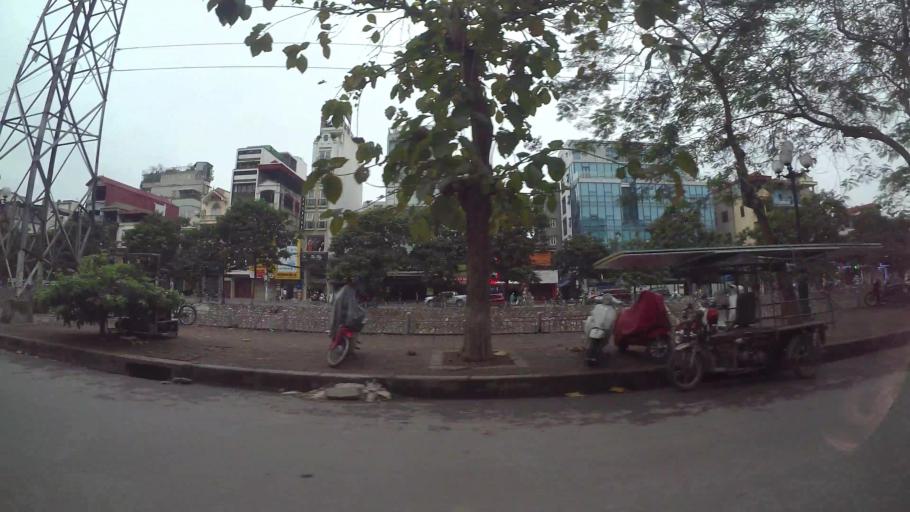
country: VN
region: Ha Noi
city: Hai BaTrung
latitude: 21.0044
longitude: 105.8617
